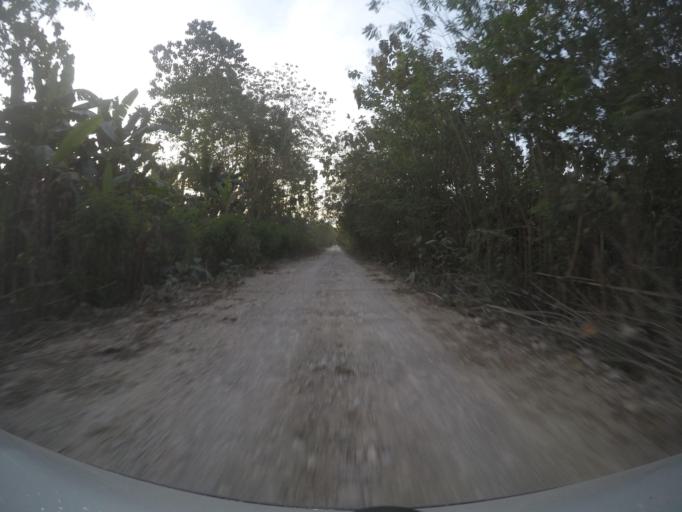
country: TL
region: Viqueque
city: Viqueque
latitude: -8.9307
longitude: 126.4102
